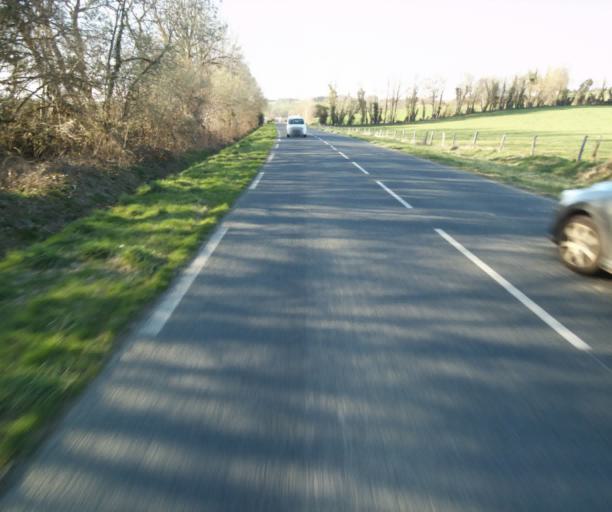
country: FR
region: Limousin
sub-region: Departement de la Correze
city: Chamboulive
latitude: 45.4126
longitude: 1.7160
